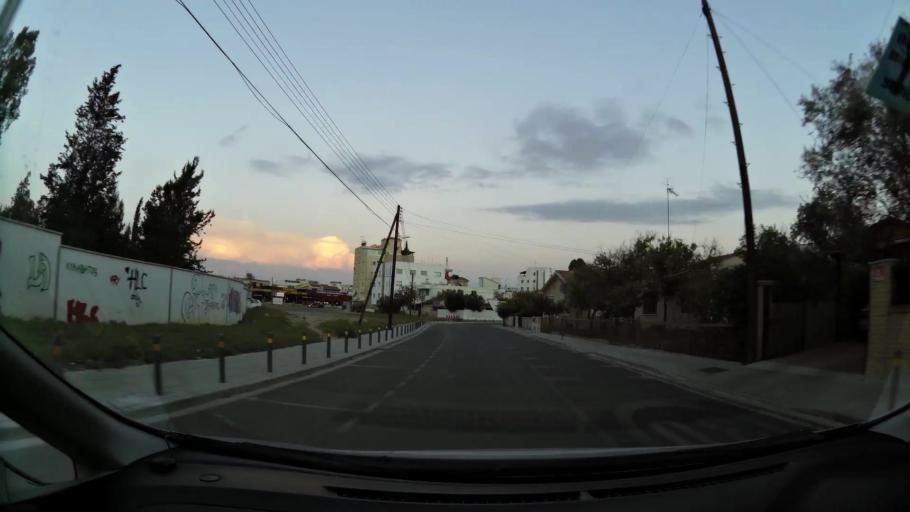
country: CY
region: Lefkosia
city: Nicosia
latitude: 35.1650
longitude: 33.3807
